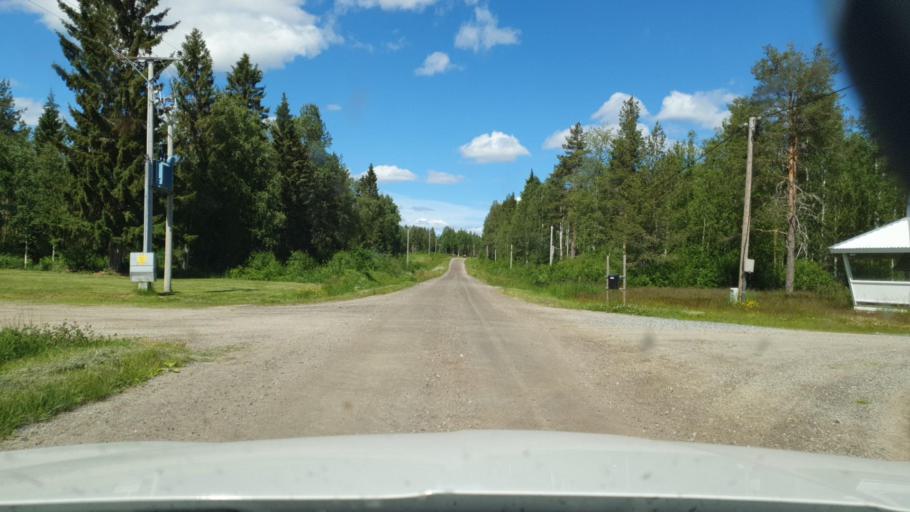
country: SE
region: Vaesterbotten
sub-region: Skelleftea Kommun
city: Backa
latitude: 65.1507
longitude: 21.1636
